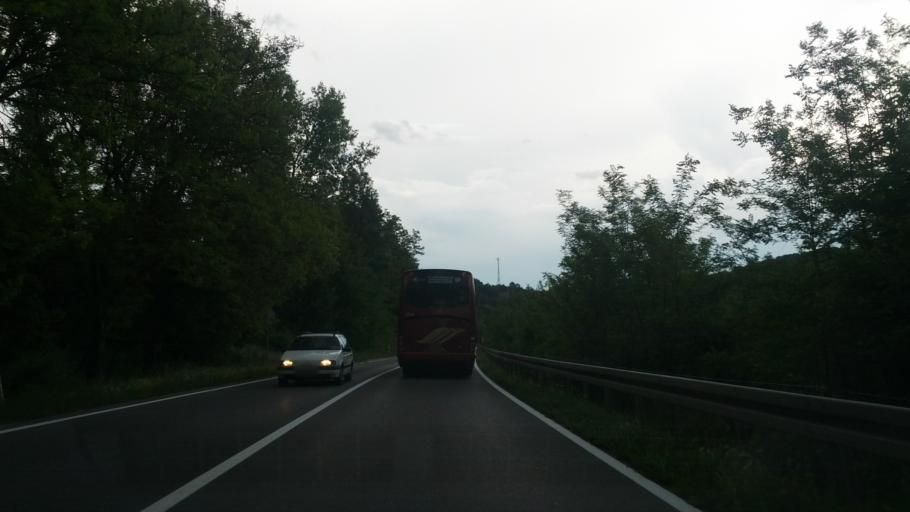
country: HR
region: Karlovacka
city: Vojnic
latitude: 45.3060
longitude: 15.6113
